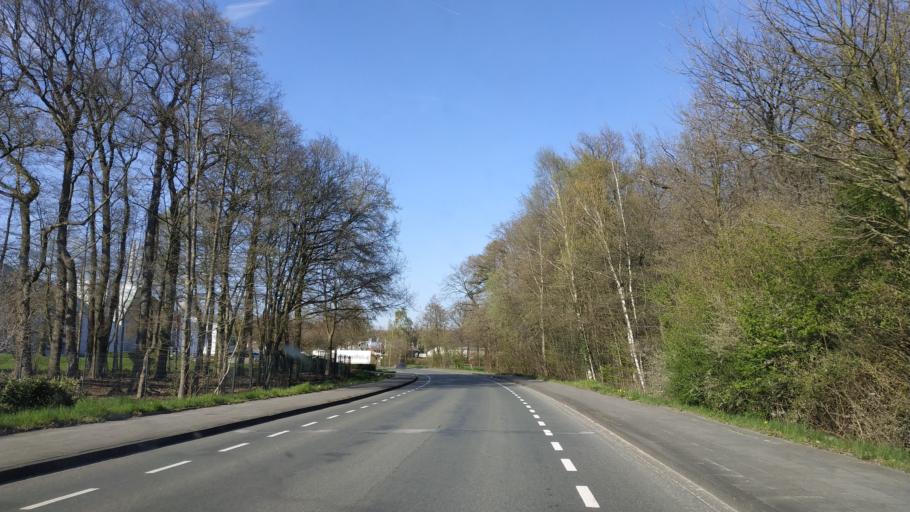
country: DE
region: North Rhine-Westphalia
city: Ibbenburen
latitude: 52.2674
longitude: 7.7451
